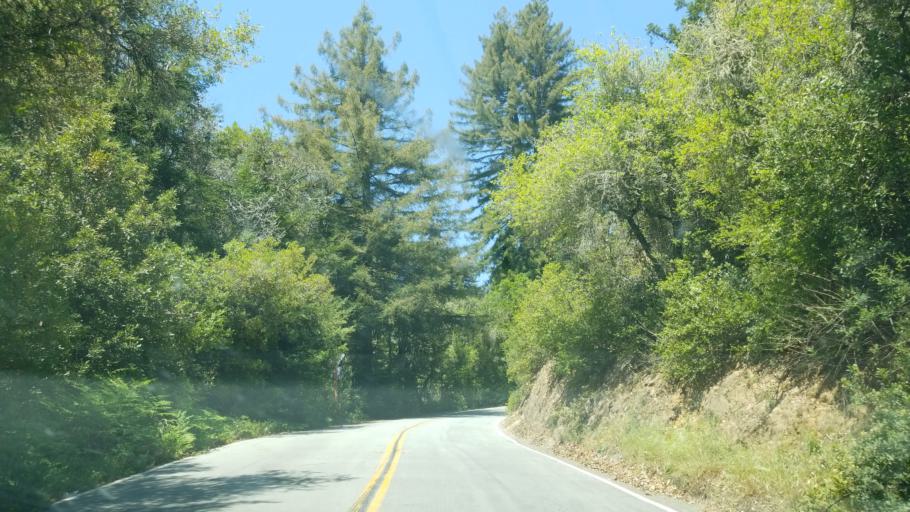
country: US
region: California
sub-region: Santa Cruz County
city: Interlaken
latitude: 37.0091
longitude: -121.7107
